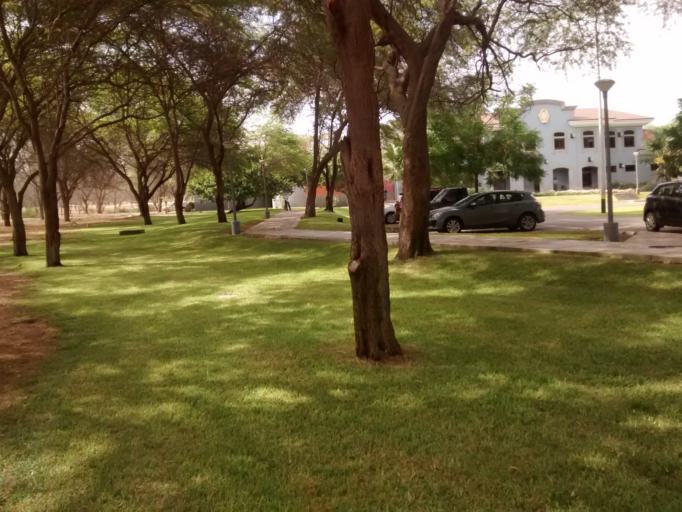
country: PE
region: Piura
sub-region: Provincia de Piura
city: Piura
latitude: -5.1784
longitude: -80.6363
